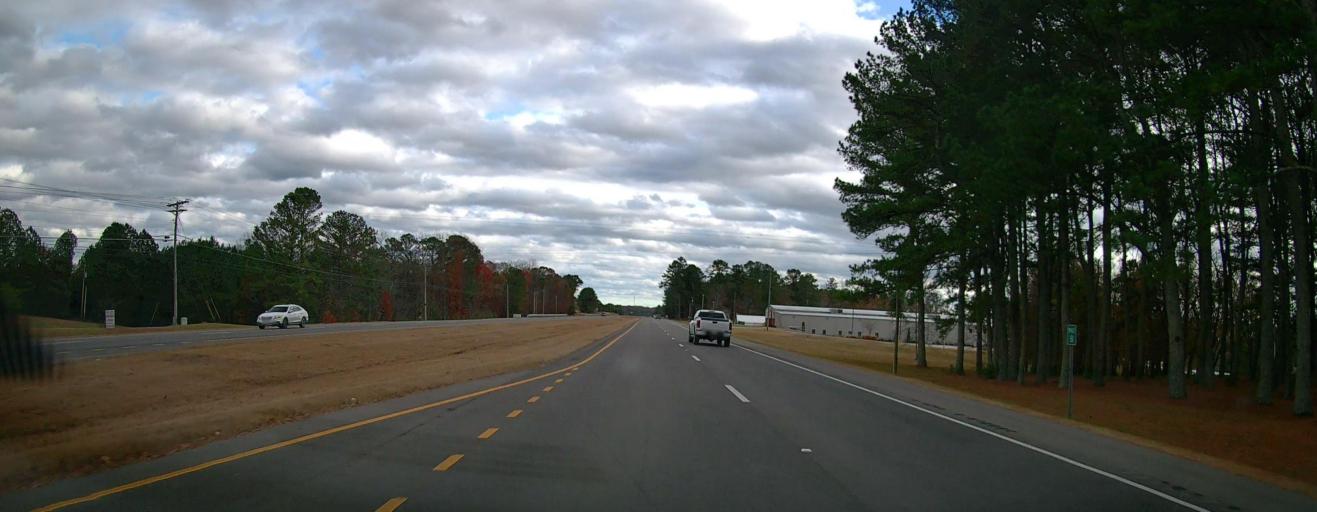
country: US
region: Alabama
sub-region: Cullman County
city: Cullman
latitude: 34.2244
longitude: -86.9020
